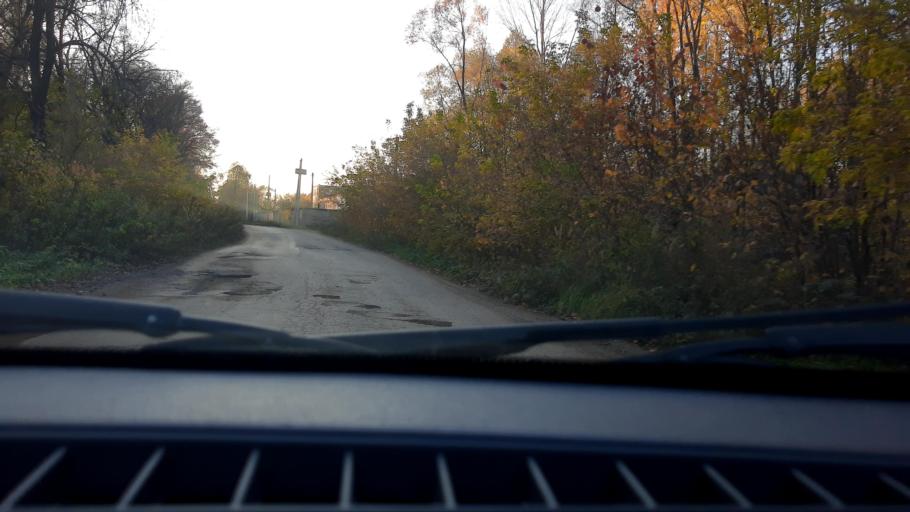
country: RU
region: Bashkortostan
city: Ufa
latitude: 54.7990
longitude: 56.1724
